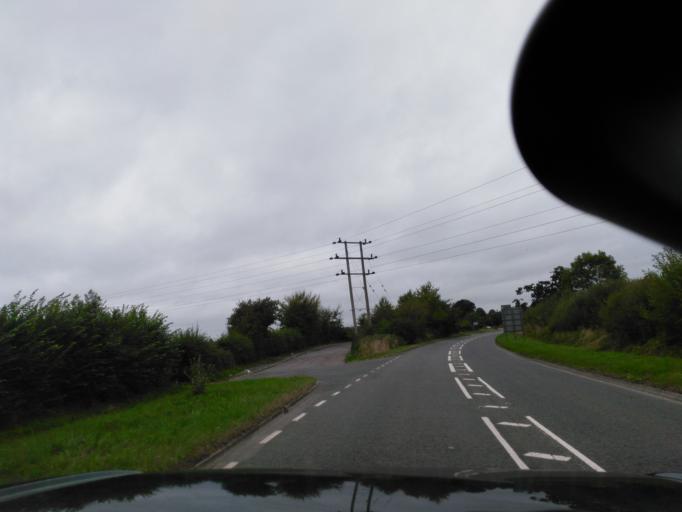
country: GB
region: England
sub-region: Wiltshire
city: Westbury
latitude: 51.2746
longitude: -2.1792
